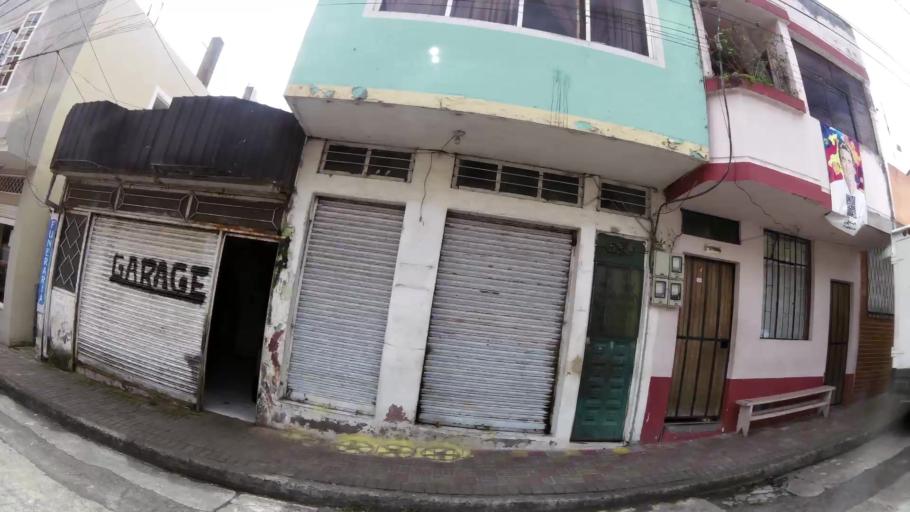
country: EC
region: Tungurahua
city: Banos
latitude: -1.3968
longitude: -78.4248
